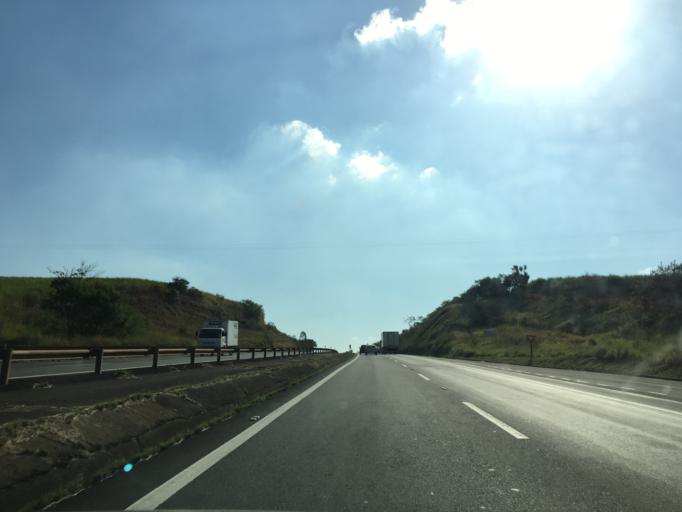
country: BR
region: Sao Paulo
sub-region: Piracicaba
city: Piracicaba
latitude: -22.7290
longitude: -47.5461
